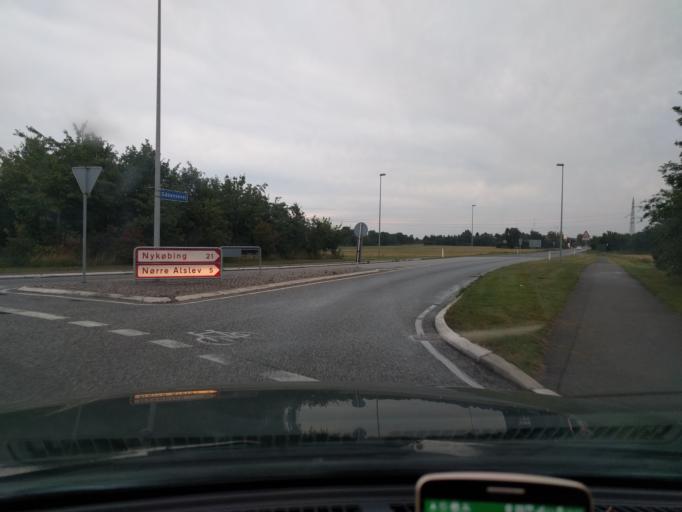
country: DK
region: Zealand
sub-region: Guldborgsund Kommune
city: Norre Alslev
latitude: 54.9460
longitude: 11.8611
